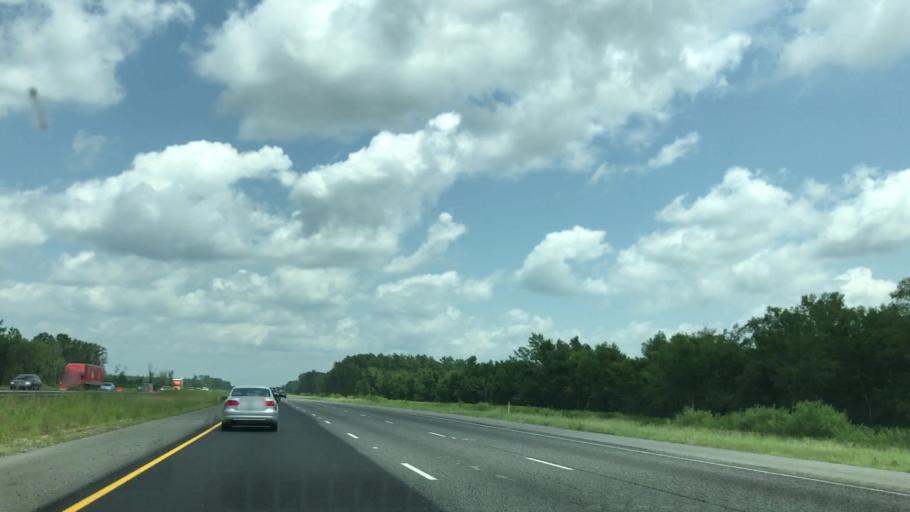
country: US
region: Georgia
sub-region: Camden County
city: Woodbine
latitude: 30.9921
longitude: -81.6661
